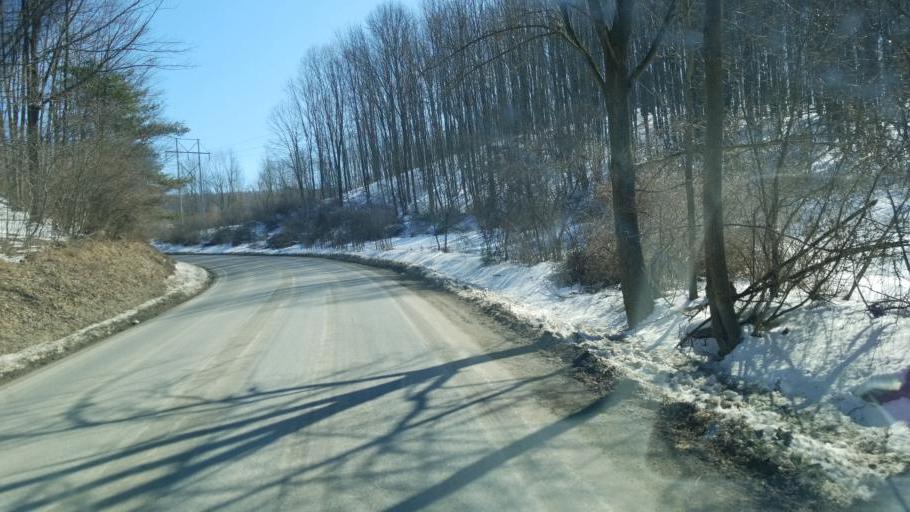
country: US
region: New York
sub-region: Allegany County
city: Alfred
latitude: 42.2664
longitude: -77.7557
